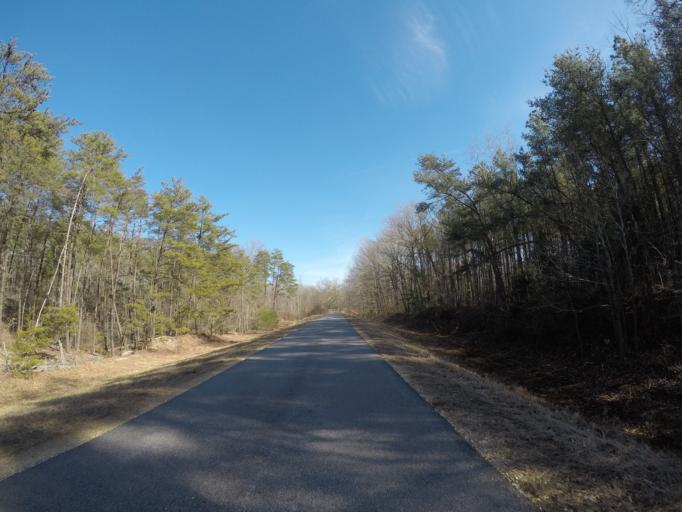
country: US
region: Maryland
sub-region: Charles County
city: Saint Charles
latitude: 38.5970
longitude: -76.9569
